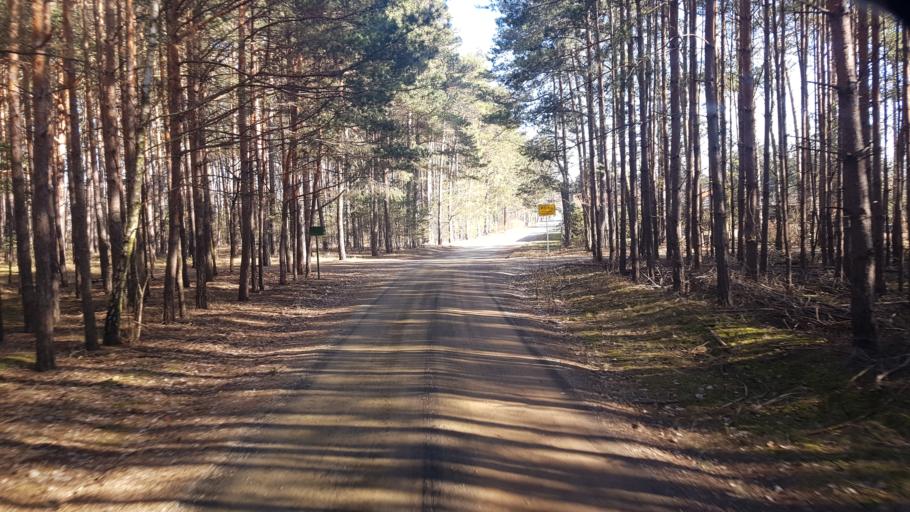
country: DE
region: Brandenburg
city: Lebusa
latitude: 51.8150
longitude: 13.3917
